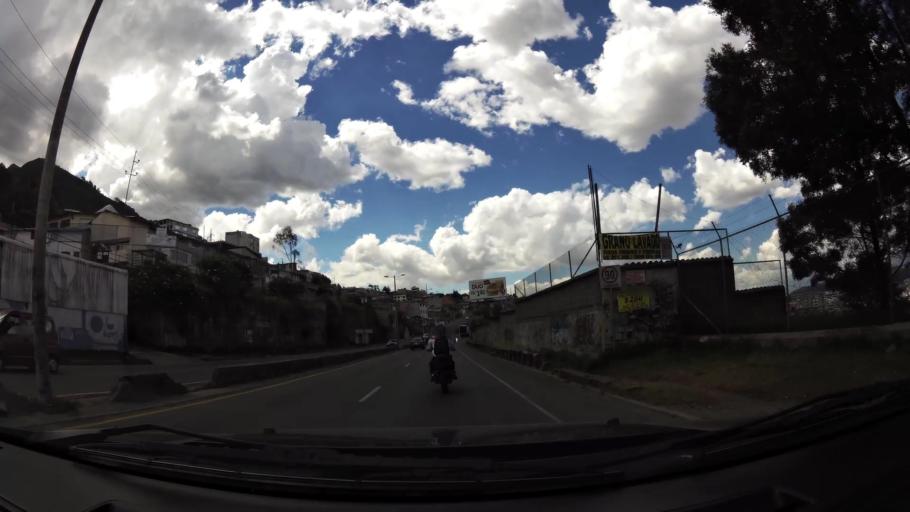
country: EC
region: Pichincha
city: Quito
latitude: -0.1879
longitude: -78.5113
